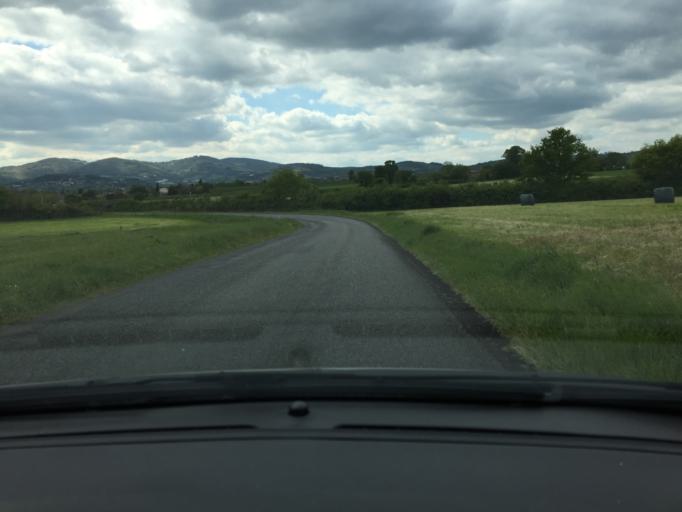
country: FR
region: Rhone-Alpes
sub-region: Departement du Rhone
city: Mornant
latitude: 45.6243
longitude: 4.6982
